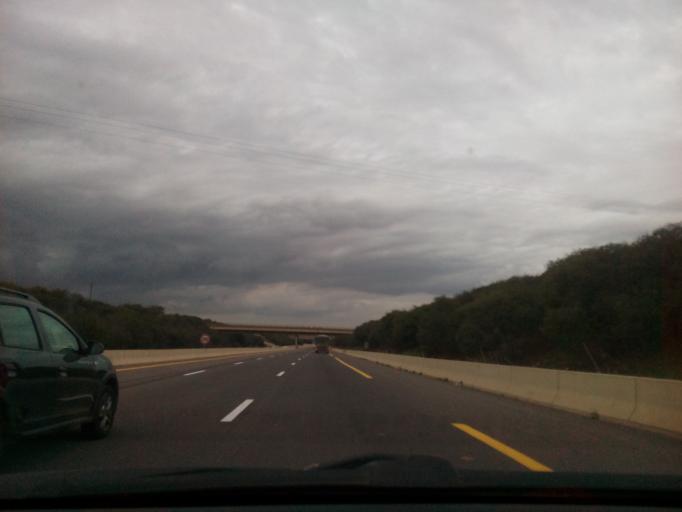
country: DZ
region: Mascara
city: Sig
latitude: 35.5372
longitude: -0.3468
